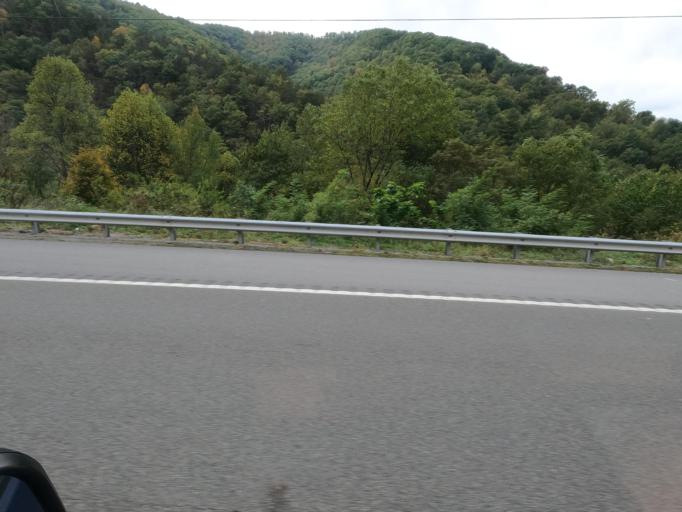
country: US
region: Tennessee
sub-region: Carter County
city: Elizabethton
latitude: 36.2970
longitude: -82.1826
